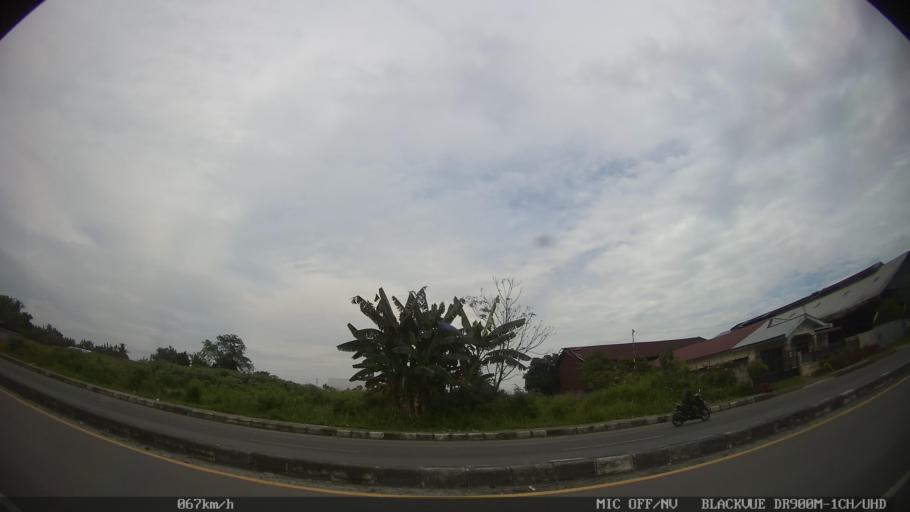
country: ID
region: North Sumatra
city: Sunggal
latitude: 3.6148
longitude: 98.5759
